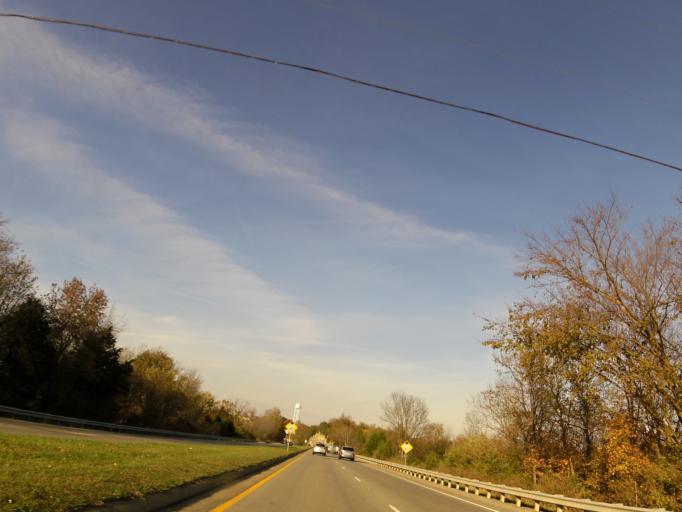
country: US
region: Kentucky
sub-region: Lincoln County
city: Stanford
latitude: 37.5250
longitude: -84.6561
